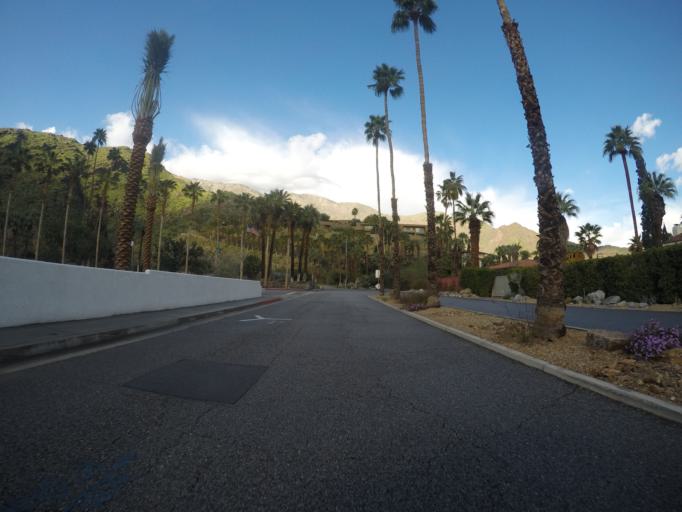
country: US
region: California
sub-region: Riverside County
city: Palm Springs
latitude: 33.8311
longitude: -116.5523
